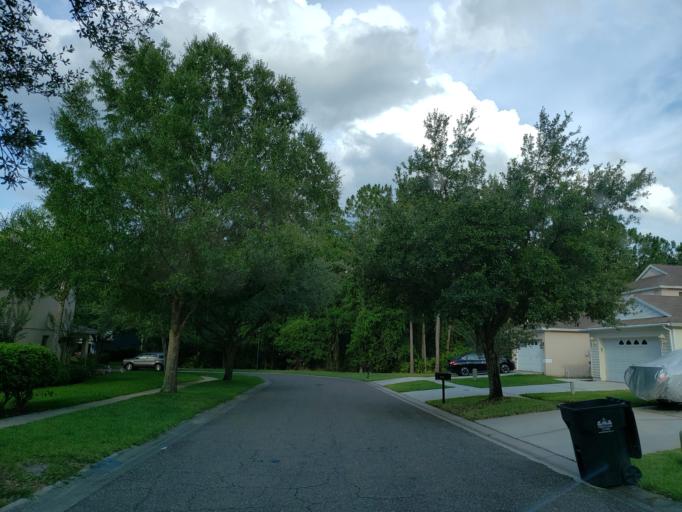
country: US
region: Florida
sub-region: Hillsborough County
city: Fish Hawk
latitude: 27.8480
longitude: -82.2270
